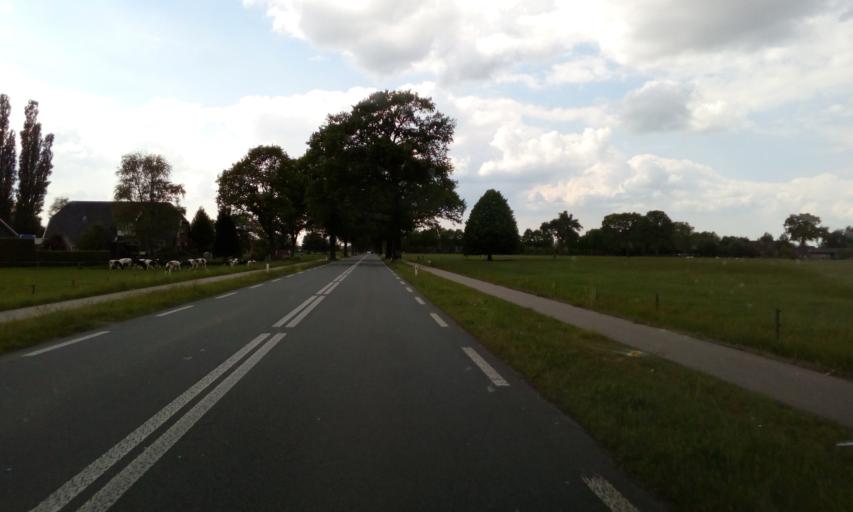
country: NL
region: Gelderland
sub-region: Gemeente Voorst
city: Twello
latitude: 52.1900
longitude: 6.0865
